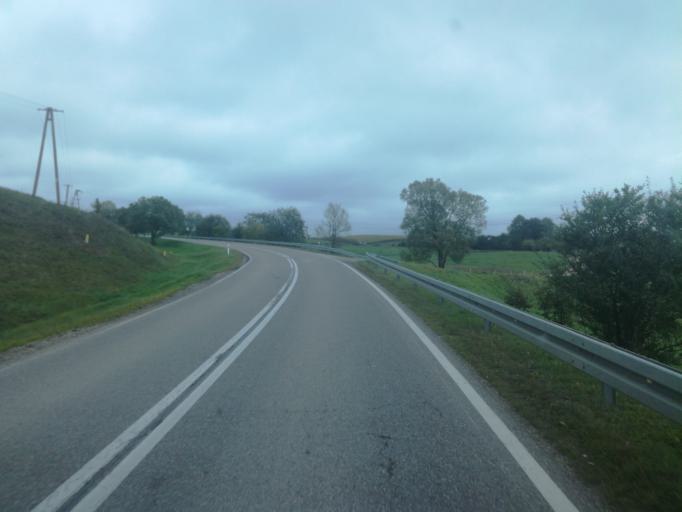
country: PL
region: Podlasie
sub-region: Powiat sejnenski
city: Sejny
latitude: 54.1163
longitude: 23.4276
